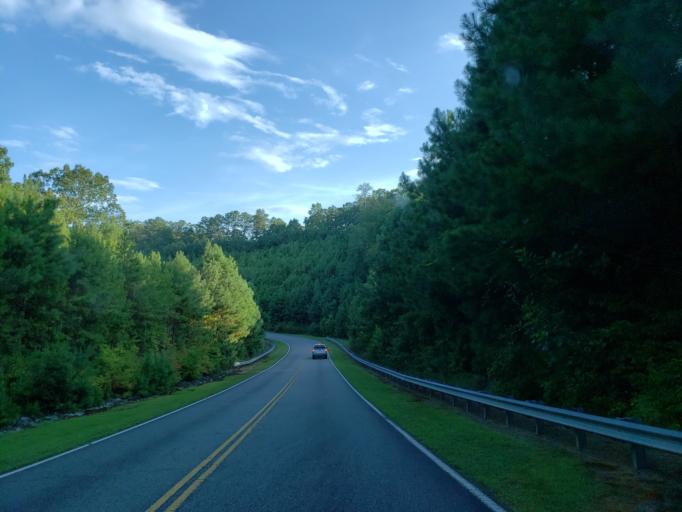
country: US
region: Georgia
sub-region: Cherokee County
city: Canton
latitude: 34.2214
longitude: -84.5736
